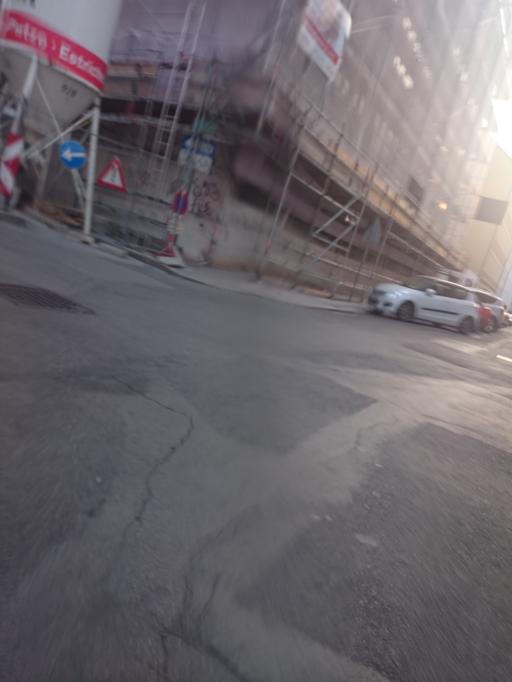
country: AT
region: Vienna
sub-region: Wien Stadt
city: Vienna
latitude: 48.2548
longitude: 16.4115
